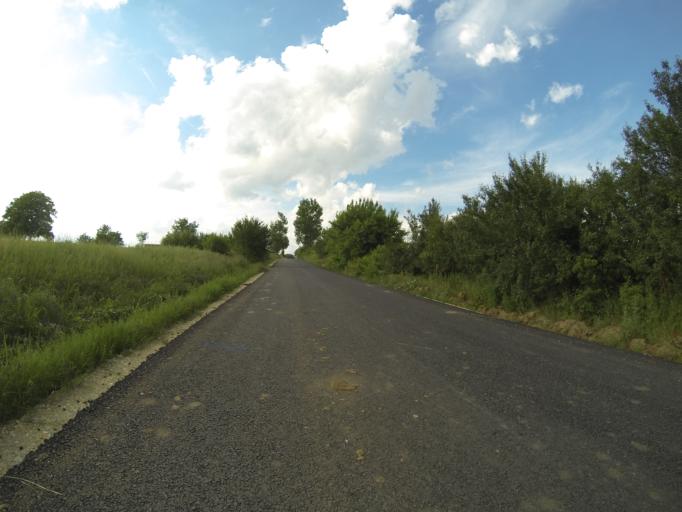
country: RO
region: Dolj
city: Satu Nou Calopar
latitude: 44.1341
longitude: 23.7958
